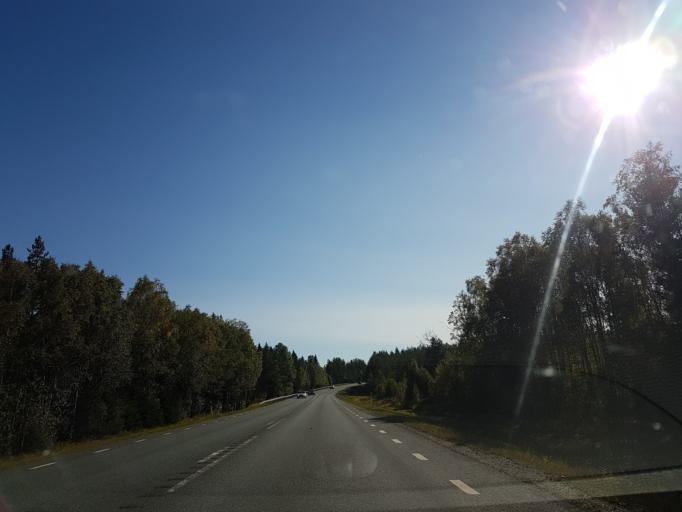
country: SE
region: Vaesterbotten
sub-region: Skelleftea Kommun
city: Burea
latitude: 64.3524
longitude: 21.2936
